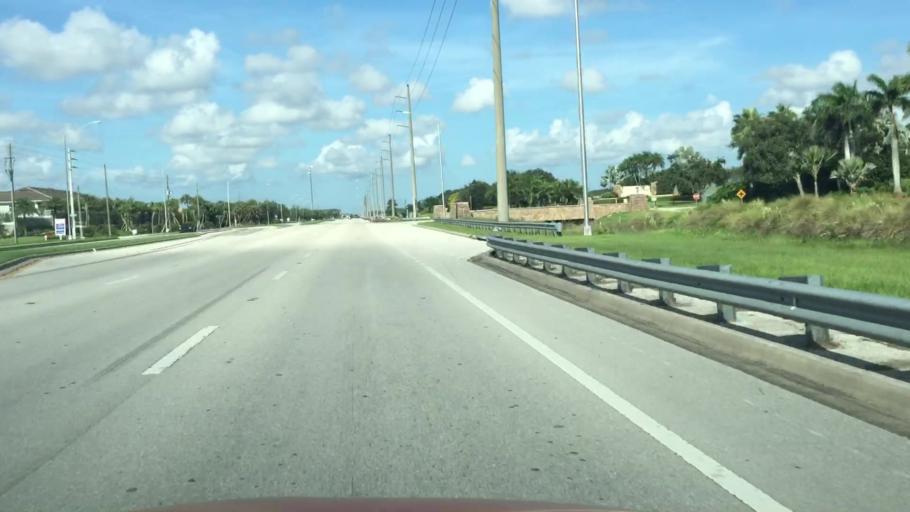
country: US
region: Florida
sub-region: Collier County
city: Vineyards
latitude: 26.2733
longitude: -81.6719
